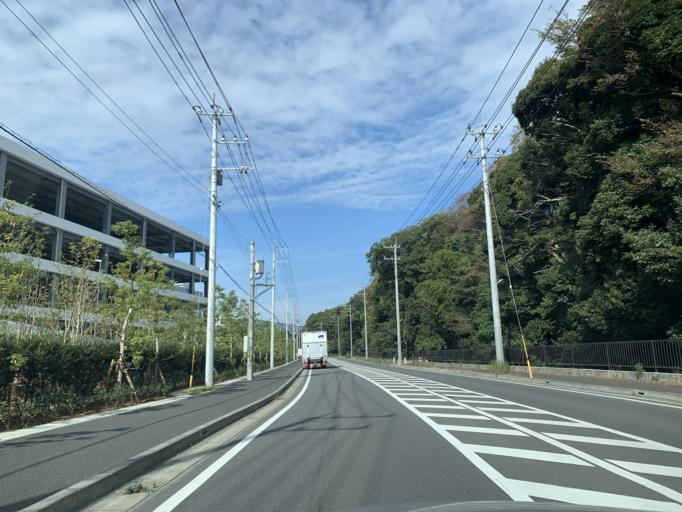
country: JP
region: Chiba
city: Nagareyama
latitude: 35.9026
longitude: 139.8948
